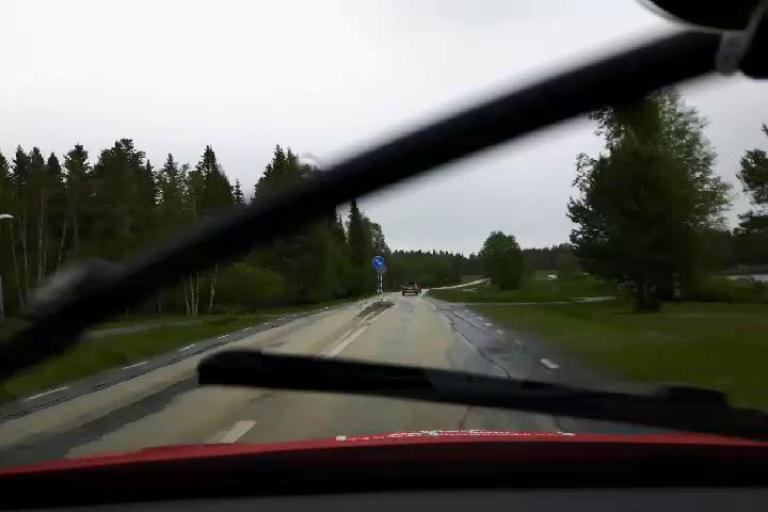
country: SE
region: Jaemtland
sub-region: Bergs Kommun
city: Hoverberg
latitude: 62.7787
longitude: 14.4313
